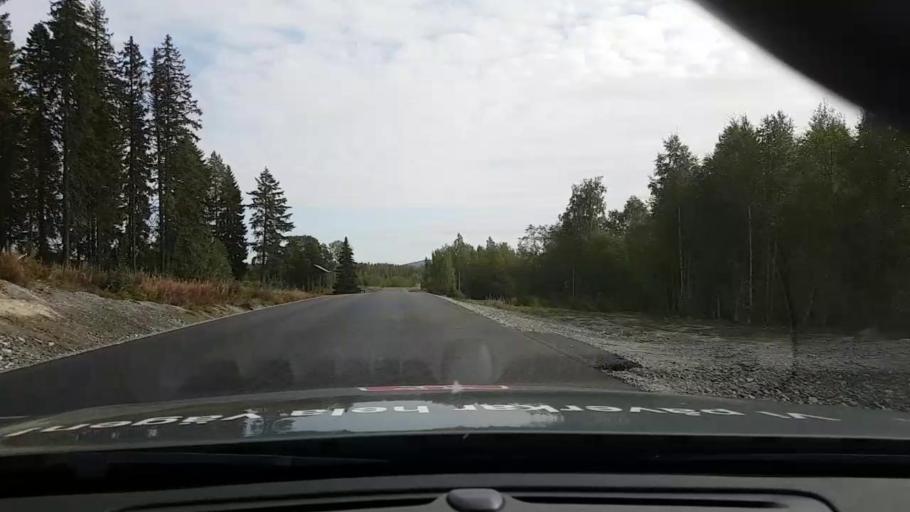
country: SE
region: Vaesternorrland
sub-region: OErnskoeldsviks Kommun
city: Bjasta
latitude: 63.2917
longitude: 18.5062
